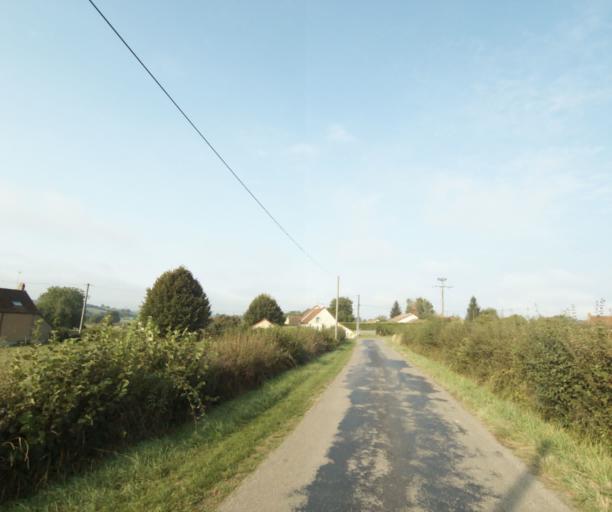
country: FR
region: Bourgogne
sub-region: Departement de Saone-et-Loire
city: Charolles
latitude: 46.4803
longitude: 4.2749
